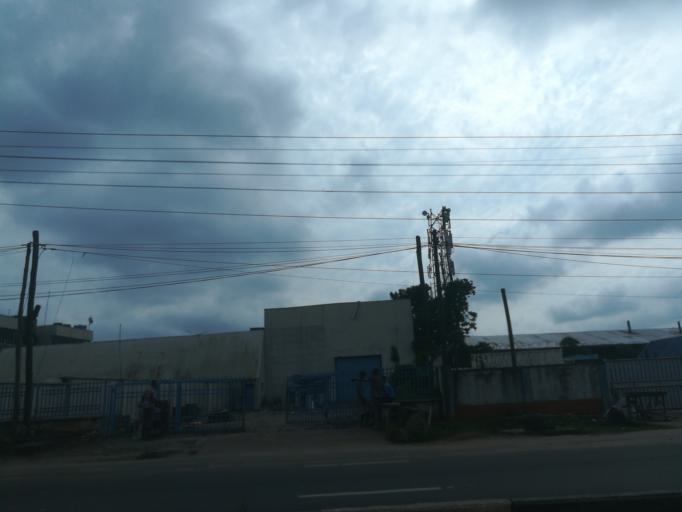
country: NG
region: Lagos
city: Ikeja
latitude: 6.6059
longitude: 3.3366
